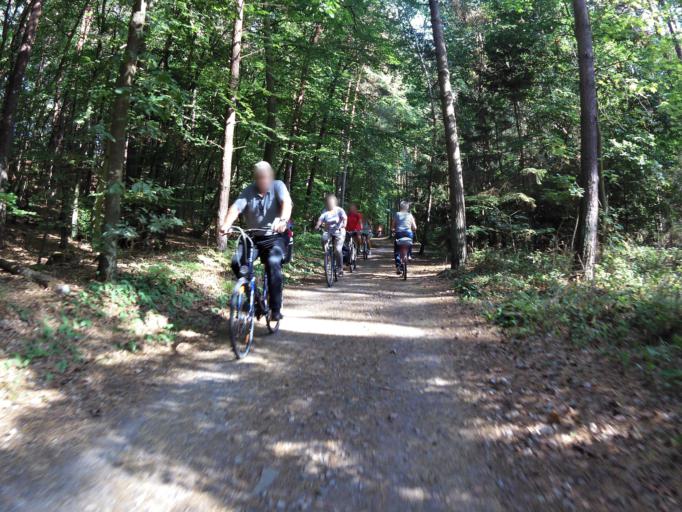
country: DE
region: Mecklenburg-Vorpommern
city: Ostseebad Zinnowitz
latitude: 54.0710
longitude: 13.9426
